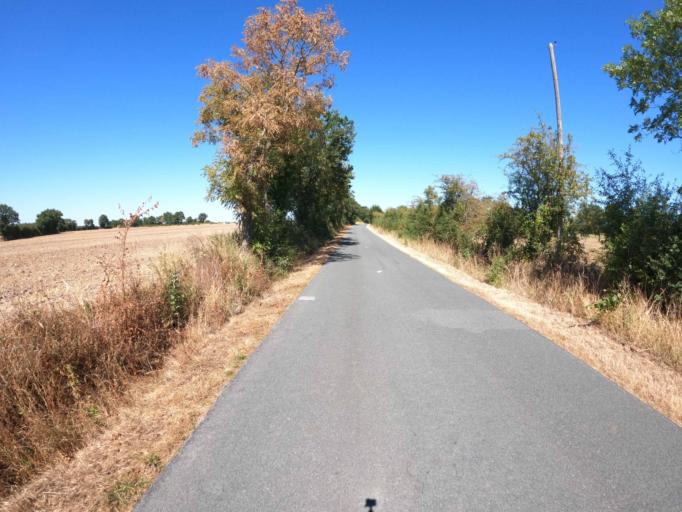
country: FR
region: Pays de la Loire
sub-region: Departement de la Vendee
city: Les Landes-Genusson
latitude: 46.9669
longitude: -1.1015
